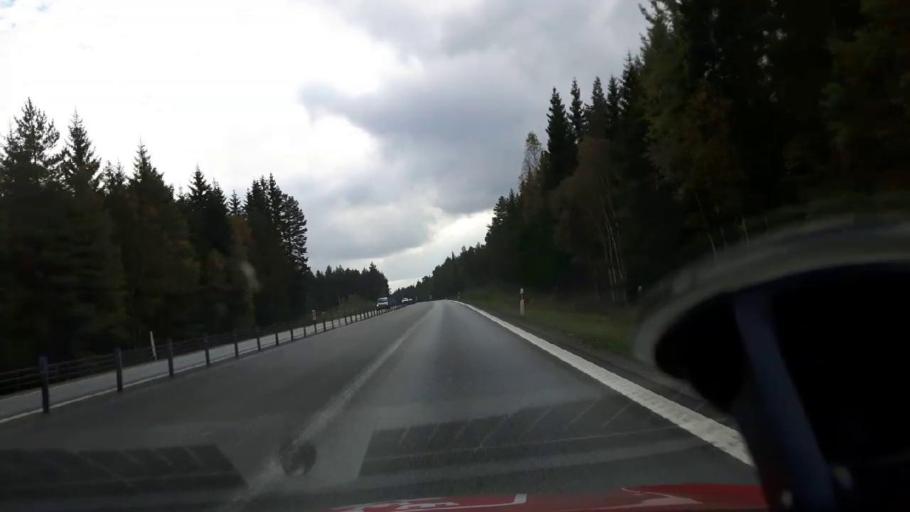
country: SE
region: Gaevleborg
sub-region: Gavle Kommun
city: Norrsundet
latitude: 60.8806
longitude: 17.0457
